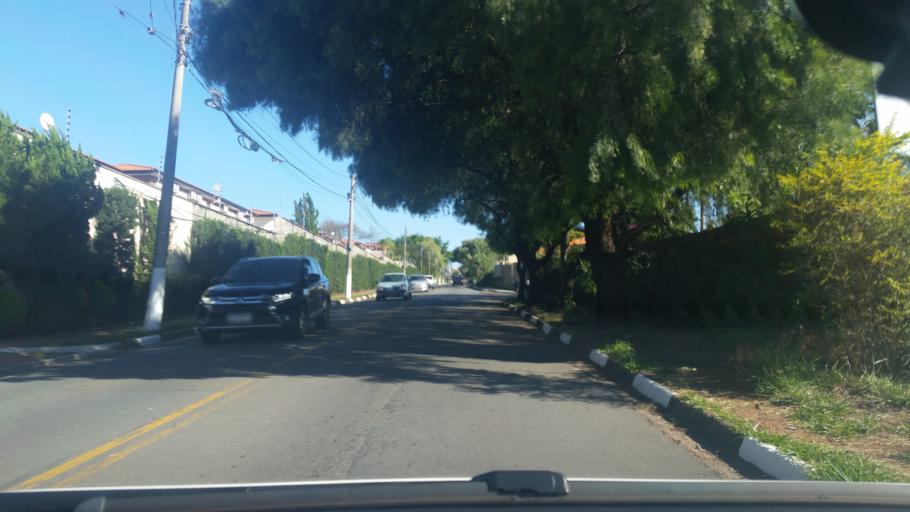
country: BR
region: Sao Paulo
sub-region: Campinas
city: Campinas
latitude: -22.8602
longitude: -47.0538
